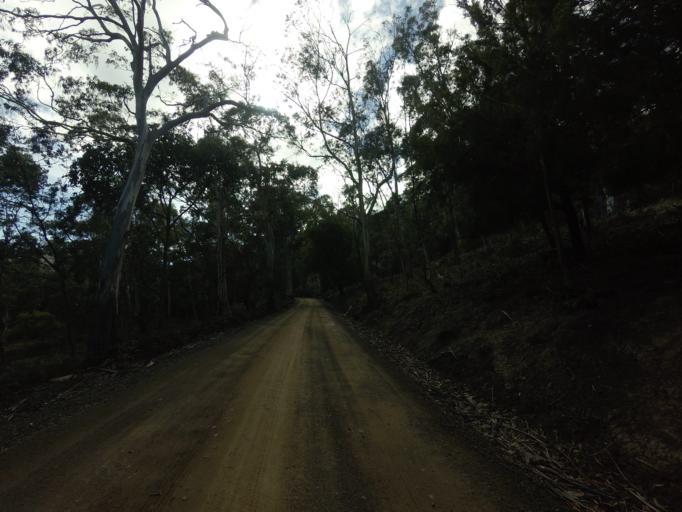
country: AU
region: Tasmania
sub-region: Clarence
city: Sandford
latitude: -43.0777
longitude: 147.6683
